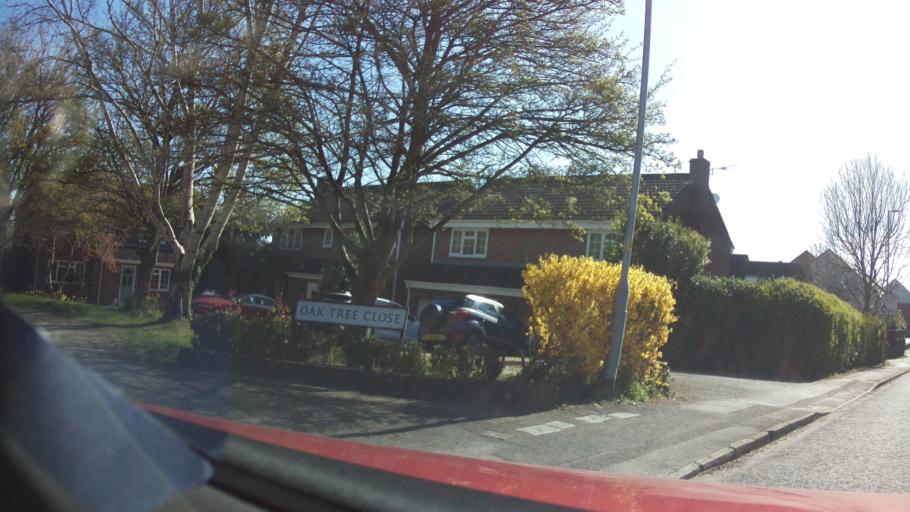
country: GB
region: England
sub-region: Wiltshire
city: Trowbridge
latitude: 51.3231
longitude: -2.2227
